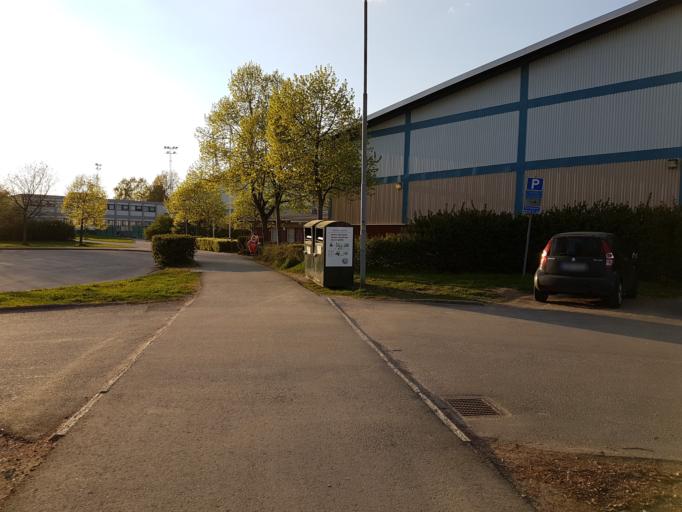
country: SE
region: Stockholm
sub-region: Solna Kommun
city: Rasunda
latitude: 59.3766
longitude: 17.9765
